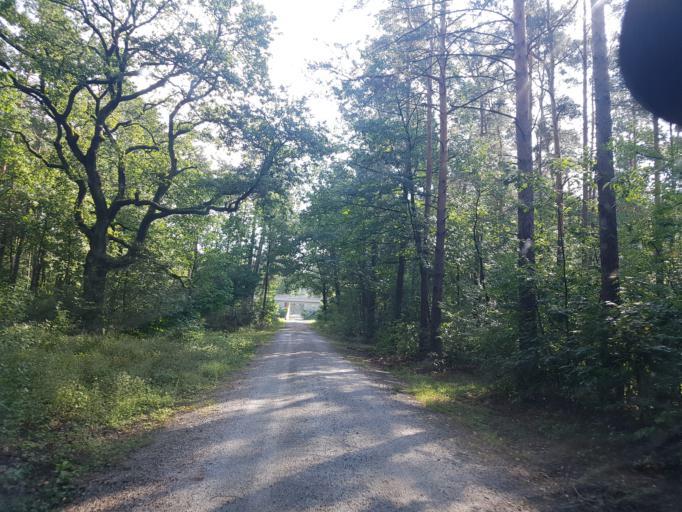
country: DE
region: Brandenburg
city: Hohenleipisch
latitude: 51.5147
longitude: 13.5739
